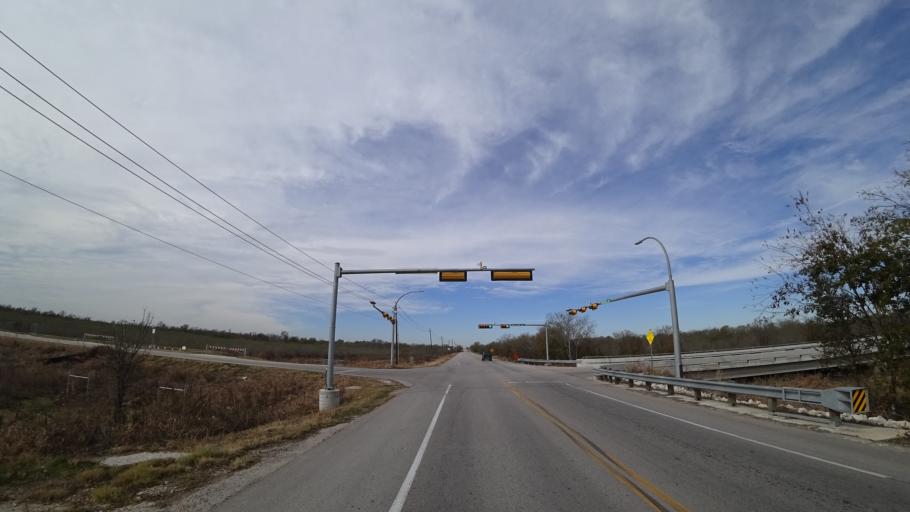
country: US
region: Texas
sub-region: Travis County
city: Garfield
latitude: 30.1635
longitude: -97.6108
